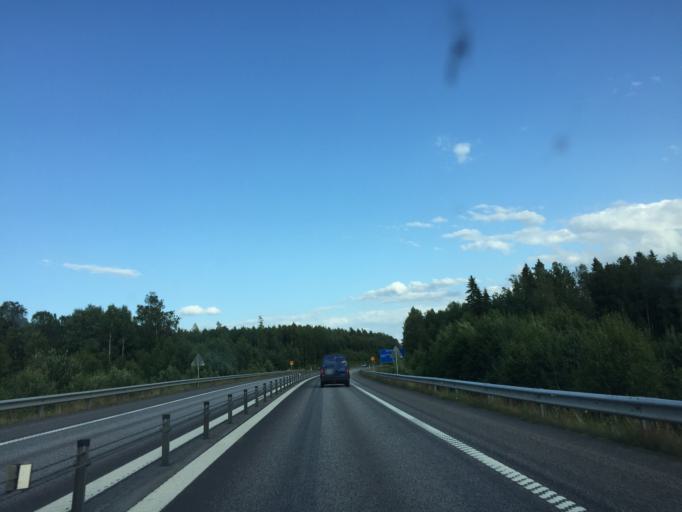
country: SE
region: OEstergoetland
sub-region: Motala Kommun
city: Motala
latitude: 58.6312
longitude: 14.9691
